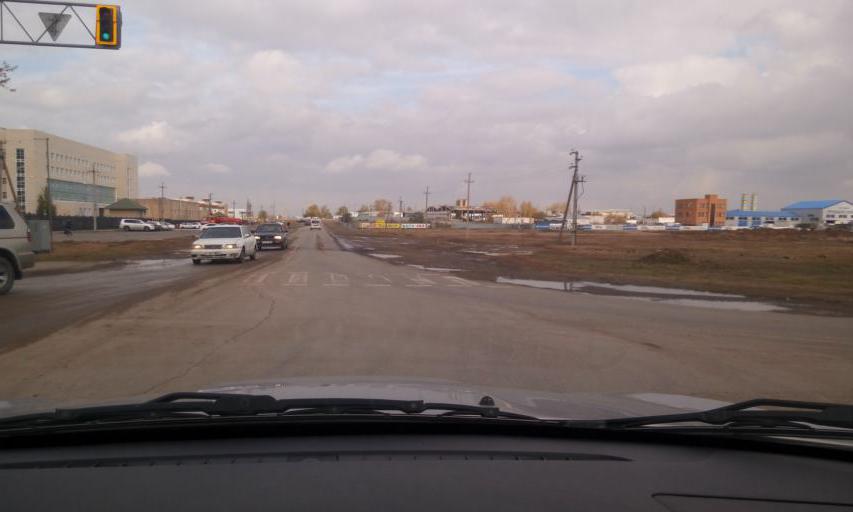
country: KZ
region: Astana Qalasy
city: Astana
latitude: 51.1382
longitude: 71.5286
